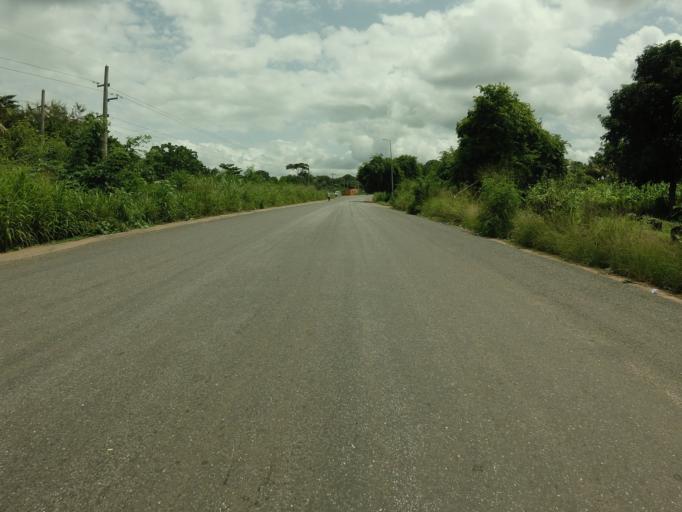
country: GH
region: Volta
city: Ho
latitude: 6.5894
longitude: 0.4755
